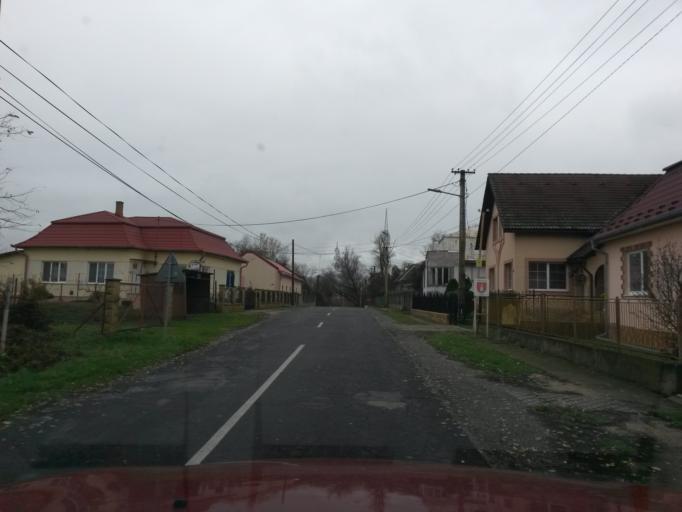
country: SK
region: Kosicky
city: Cierna nad Tisou
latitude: 48.5521
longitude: 21.9572
